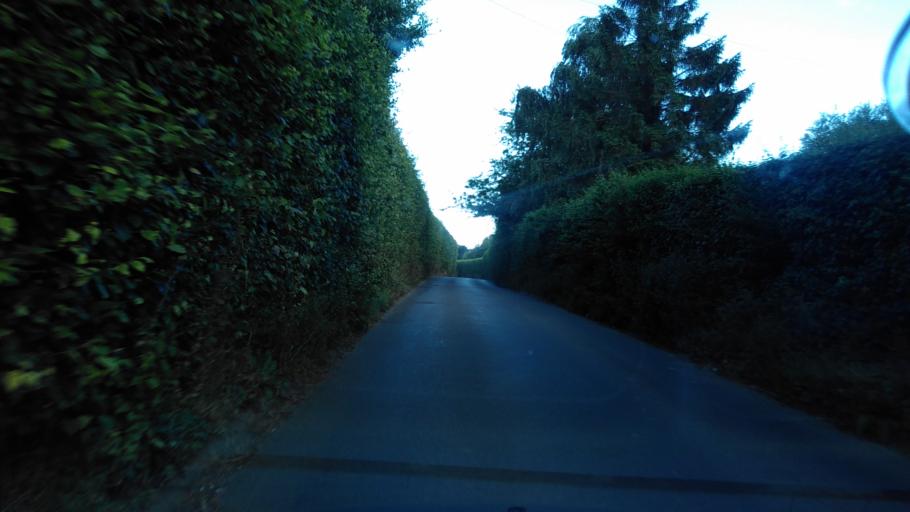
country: GB
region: England
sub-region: Kent
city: Dunkirk
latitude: 51.2698
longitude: 0.9449
